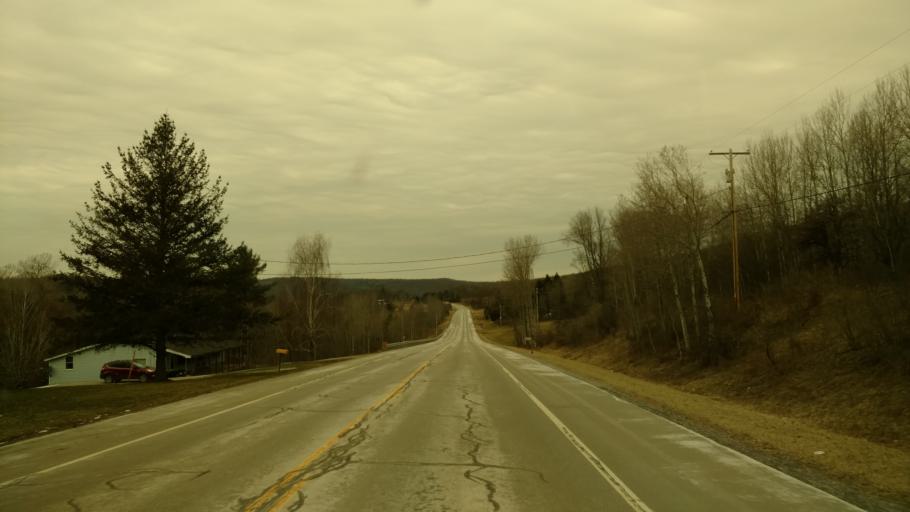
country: US
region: New York
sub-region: Allegany County
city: Wellsville
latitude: 42.0290
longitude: -77.9009
